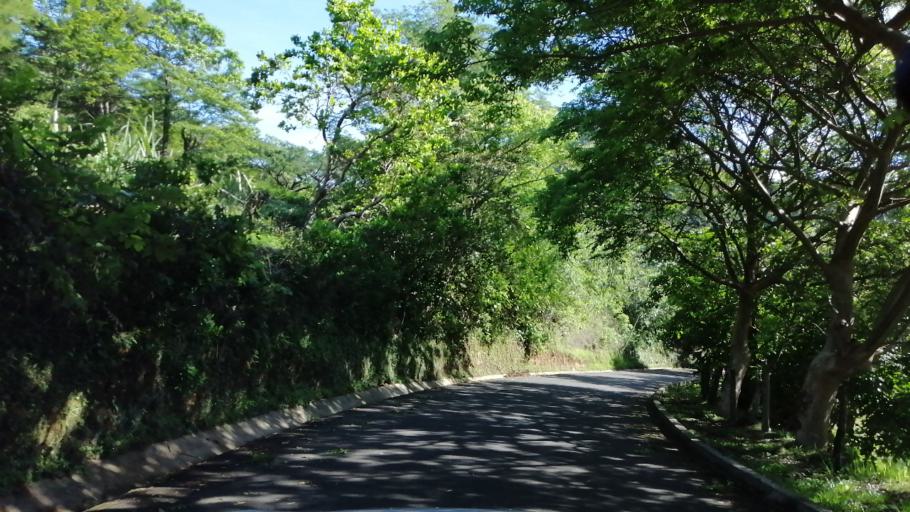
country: SV
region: Morazan
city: Corinto
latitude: 13.7909
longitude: -88.0125
